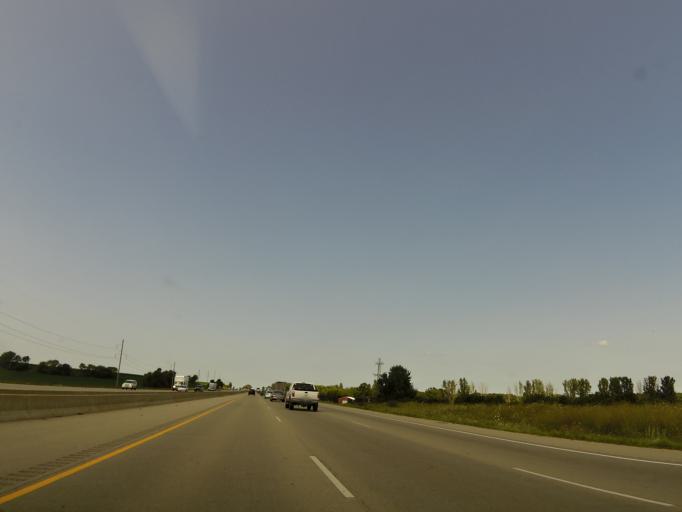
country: US
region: Wisconsin
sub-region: Dane County
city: Windsor
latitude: 43.2252
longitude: -89.3651
